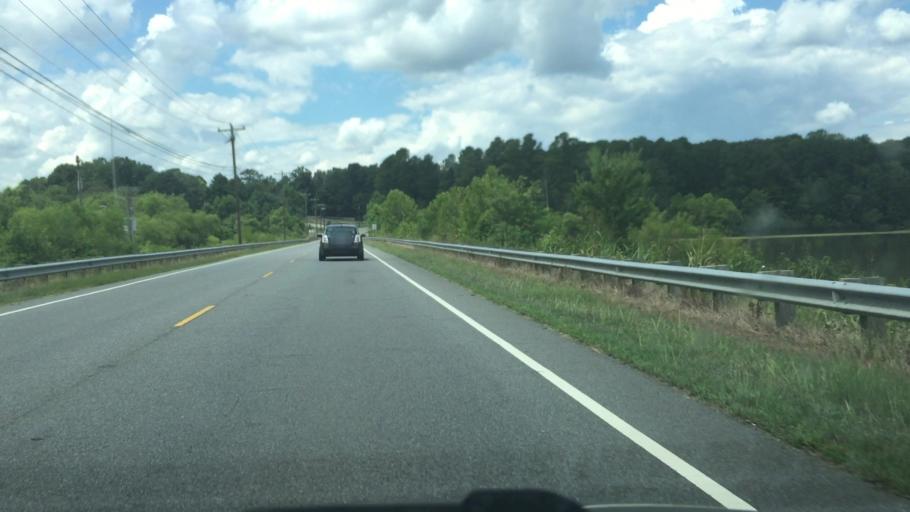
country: US
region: North Carolina
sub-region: Rowan County
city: Enochville
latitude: 35.4819
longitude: -80.7142
